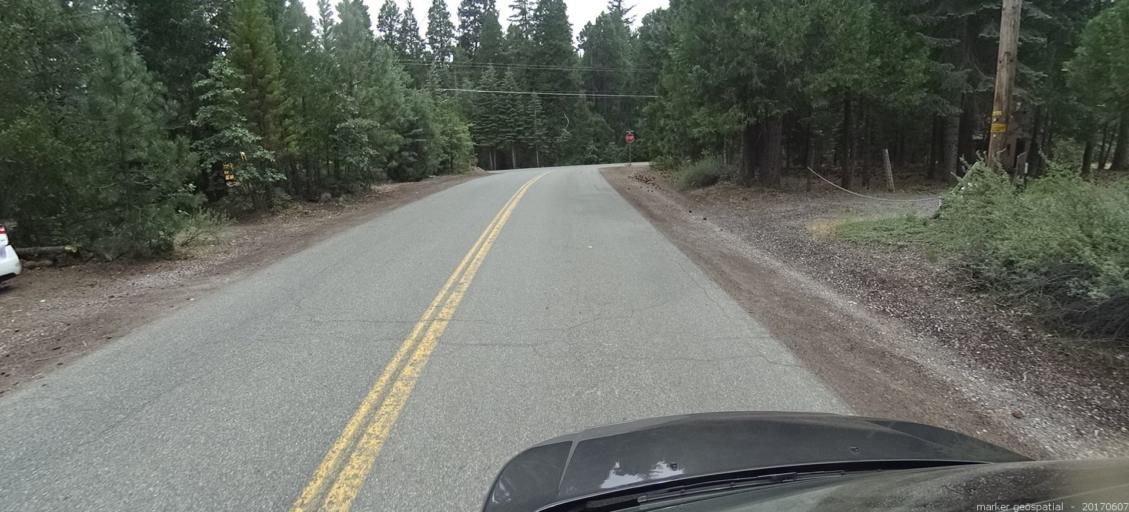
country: US
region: California
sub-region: Siskiyou County
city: Mount Shasta
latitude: 41.3348
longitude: -122.3494
